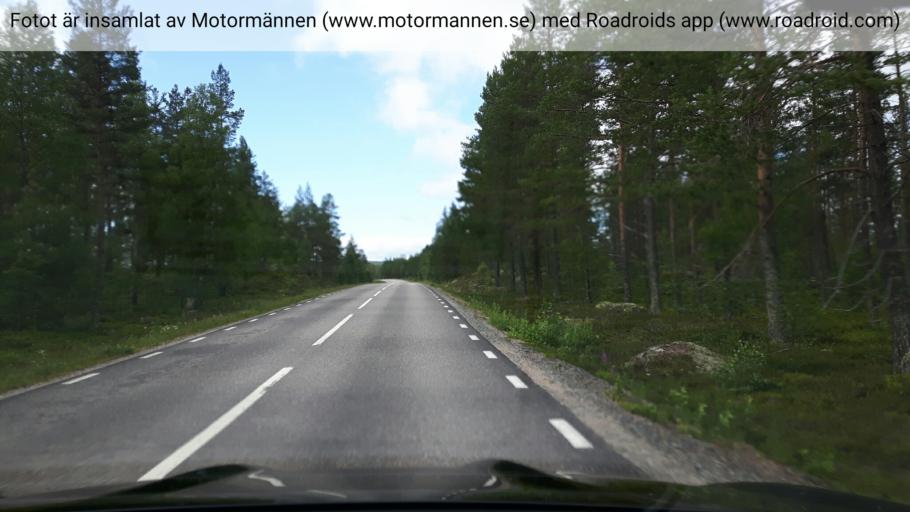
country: SE
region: Gaevleborg
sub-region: Ljusdals Kommun
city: Farila
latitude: 61.7438
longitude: 15.3558
